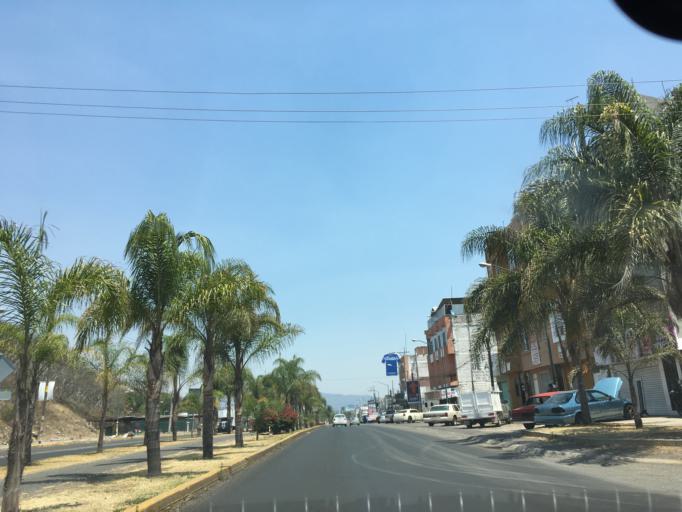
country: MX
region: Guanajuato
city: Moroleon
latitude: 20.1082
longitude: -101.1694
